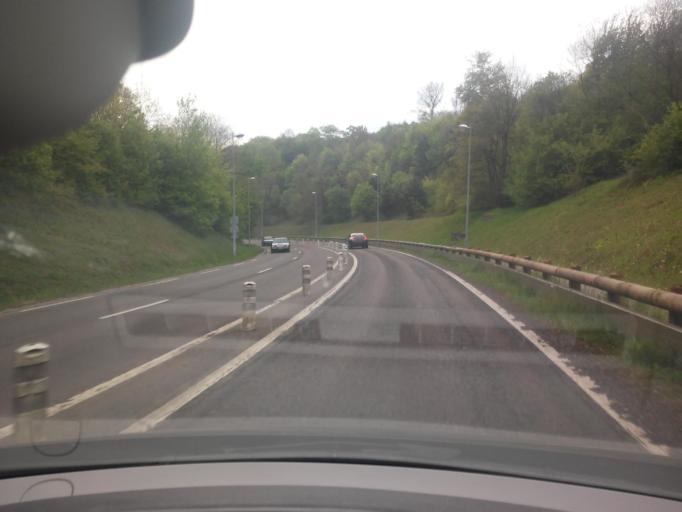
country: FR
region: Lorraine
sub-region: Departement de Meurthe-et-Moselle
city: Laxou
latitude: 48.6855
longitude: 6.1322
